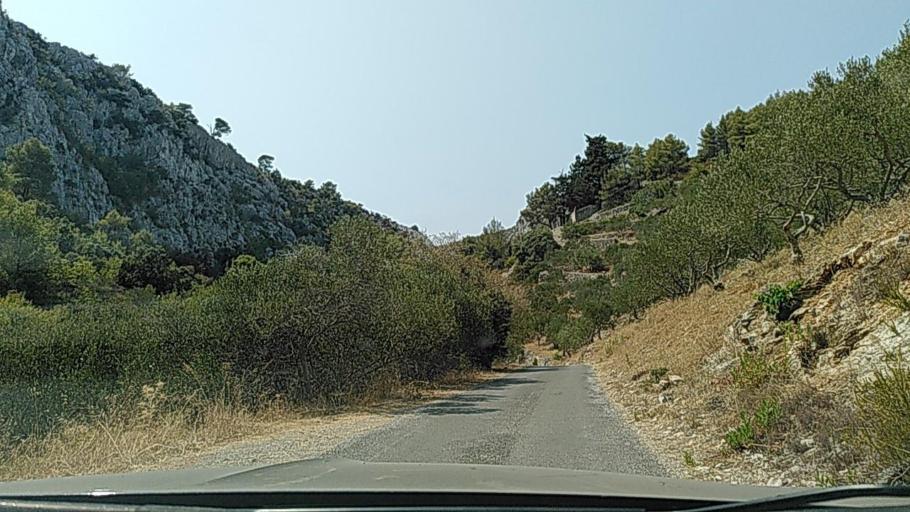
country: HR
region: Splitsko-Dalmatinska
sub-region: Grad Hvar
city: Hvar
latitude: 43.1673
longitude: 16.5064
